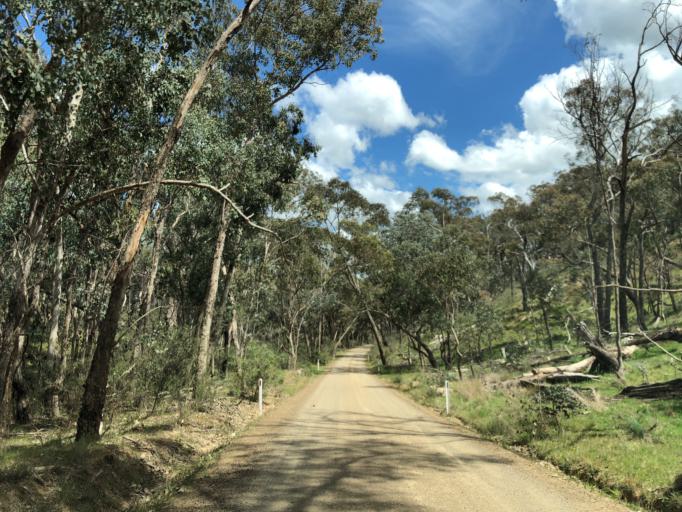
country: AU
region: Victoria
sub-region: Benalla
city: Benalla
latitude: -36.7326
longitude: 146.1435
